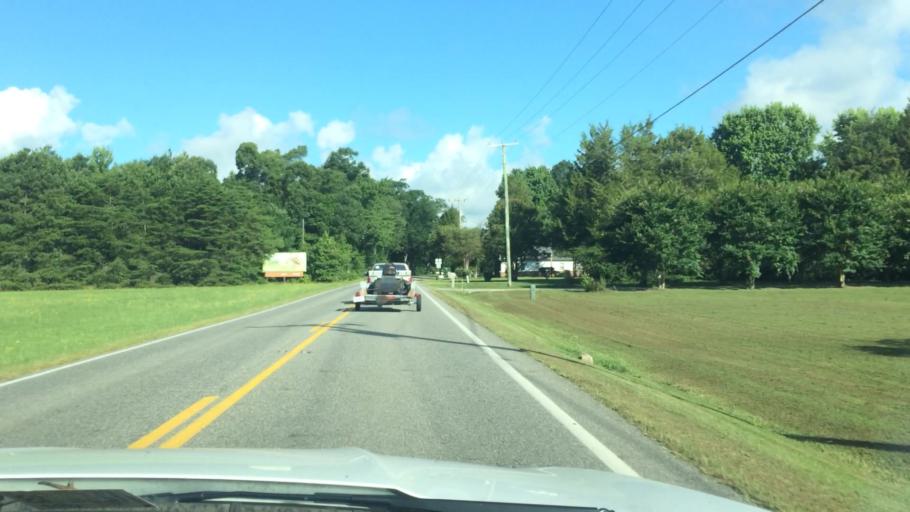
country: US
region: Virginia
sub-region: Middlesex County
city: Deltaville
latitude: 37.5388
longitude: -76.4296
